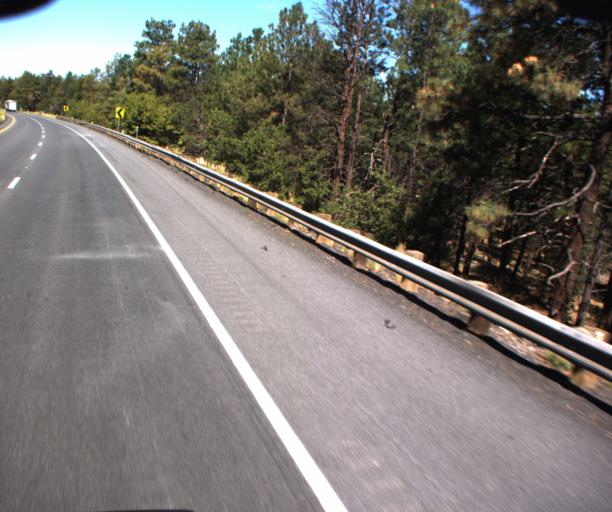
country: US
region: Arizona
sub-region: Coconino County
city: Williams
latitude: 35.2223
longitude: -112.2704
